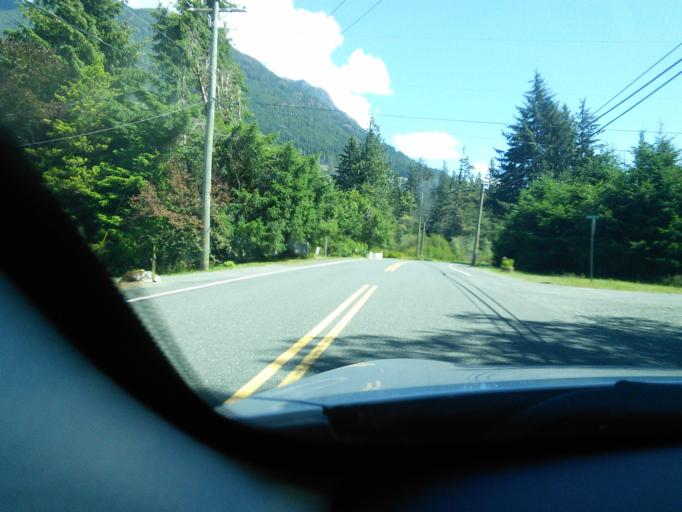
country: CA
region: British Columbia
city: Campbell River
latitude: 50.3541
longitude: -125.9096
